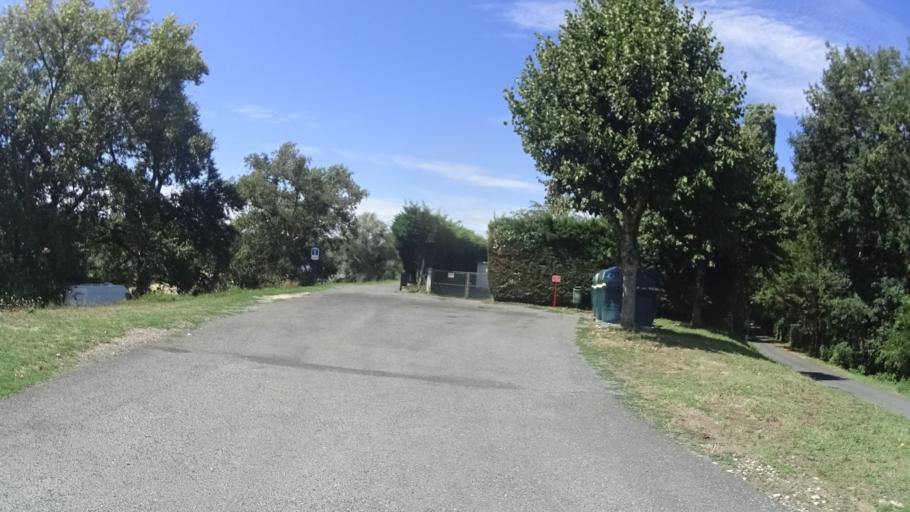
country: FR
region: Centre
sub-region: Departement du Loiret
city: Briare
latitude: 47.5903
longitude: 2.7802
